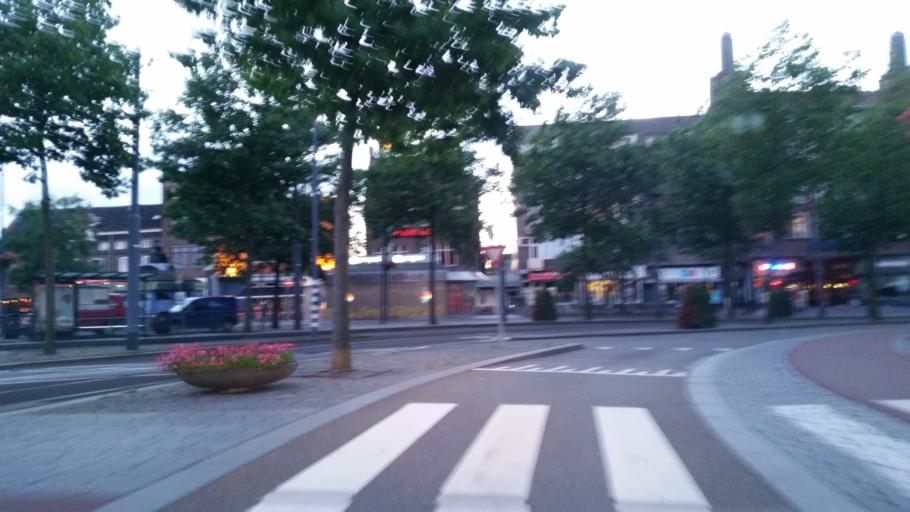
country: NL
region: South Holland
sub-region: Gemeente Schiedam
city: Schiedam
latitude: 51.9149
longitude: 4.4029
